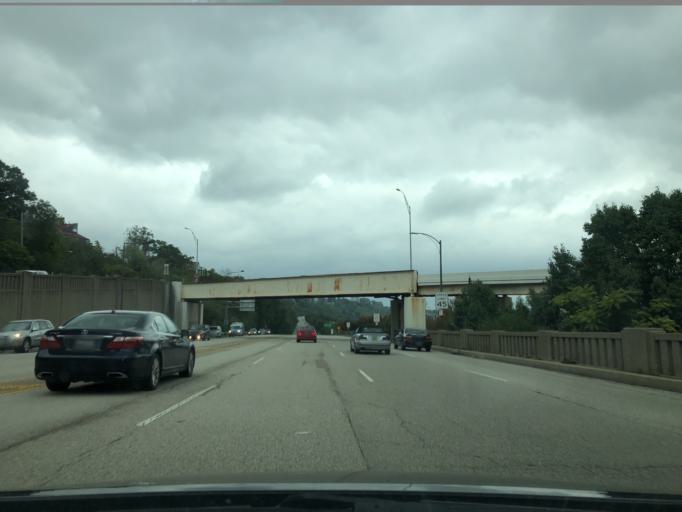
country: US
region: Kentucky
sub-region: Campbell County
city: Bellevue
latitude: 39.1070
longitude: -84.4940
